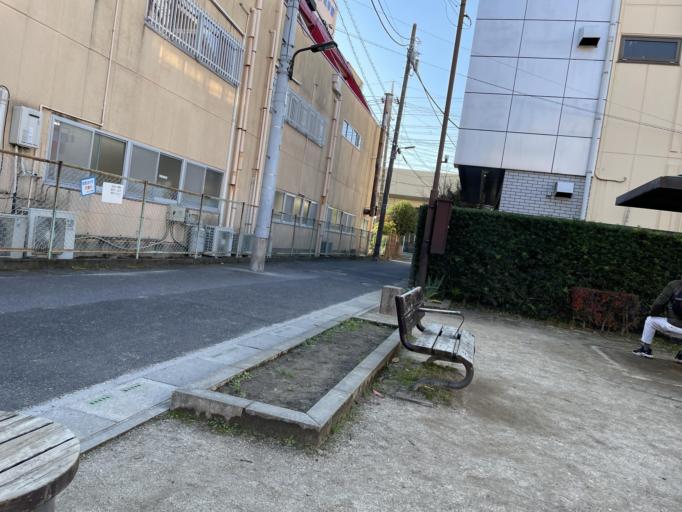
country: JP
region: Saitama
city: Soka
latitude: 35.8307
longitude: 139.8043
